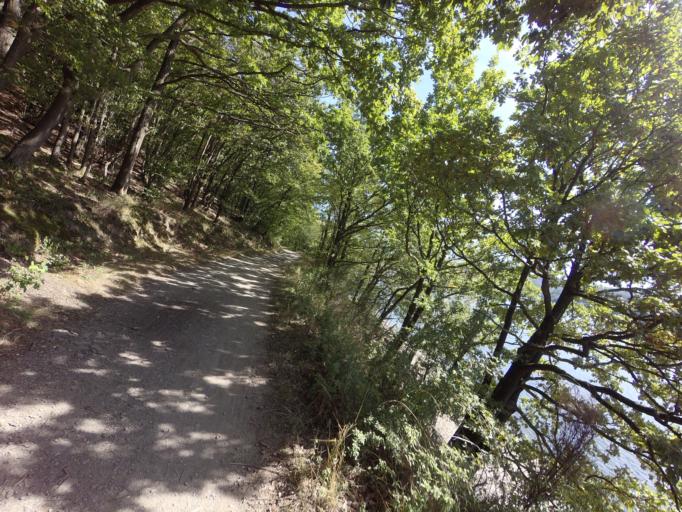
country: DE
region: North Rhine-Westphalia
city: Heimbach
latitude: 50.6476
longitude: 6.4316
